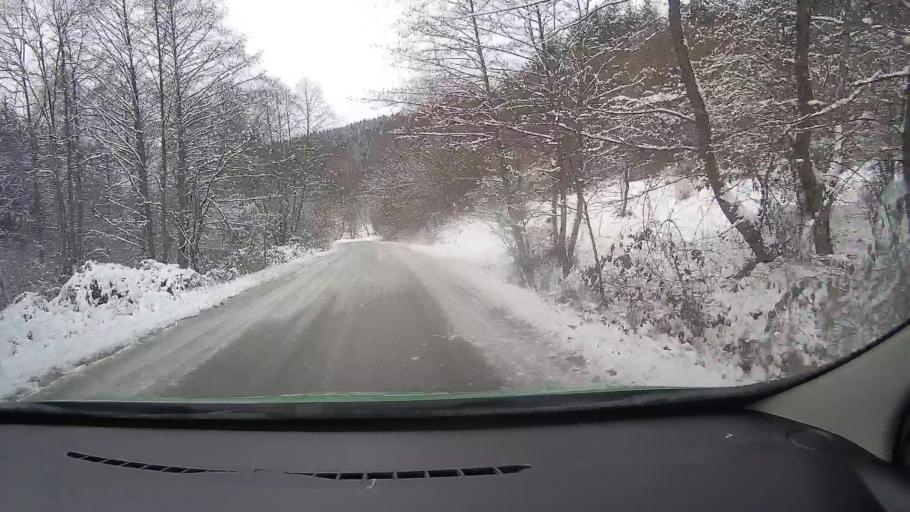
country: RO
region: Alba
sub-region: Comuna Almasu Mare
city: Almasu Mare
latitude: 46.0994
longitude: 23.1439
